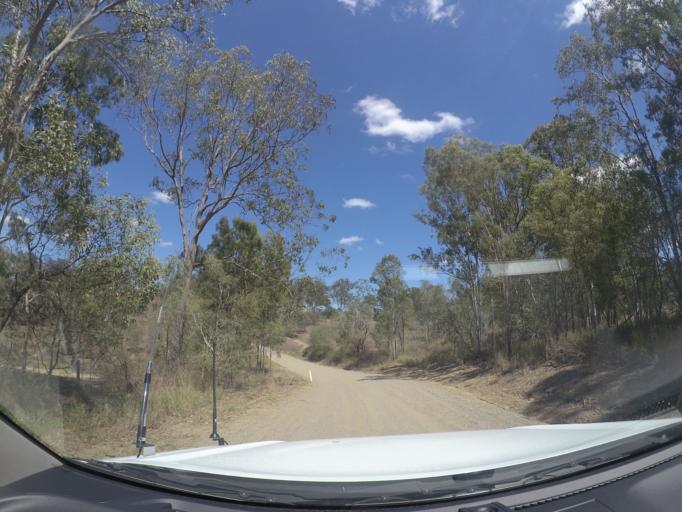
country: AU
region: Queensland
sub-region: Logan
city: Cedar Vale
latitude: -27.8467
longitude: 152.8986
